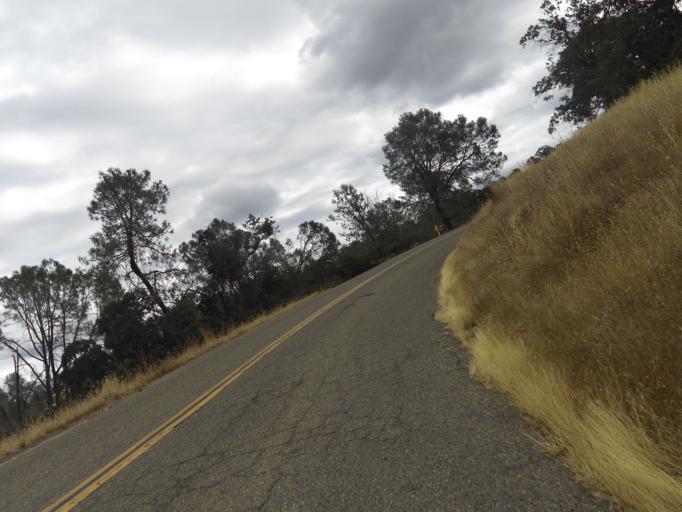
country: US
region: California
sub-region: Madera County
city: Yosemite Lakes
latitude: 37.2730
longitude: -119.8462
